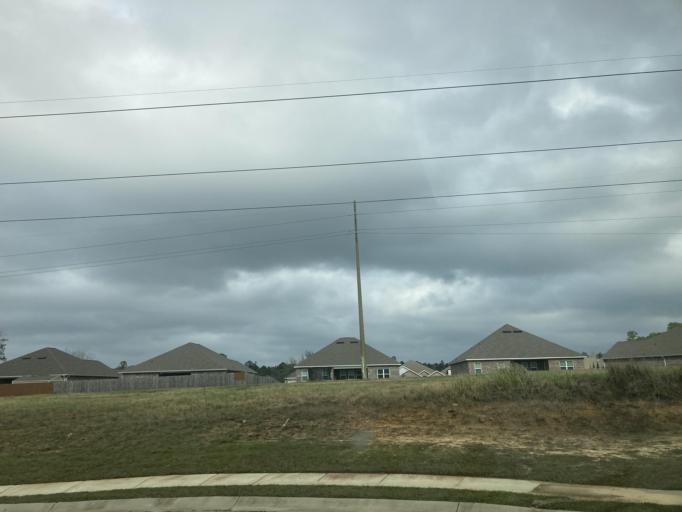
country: US
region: Mississippi
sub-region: Harrison County
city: D'Iberville
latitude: 30.4763
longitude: -88.9938
